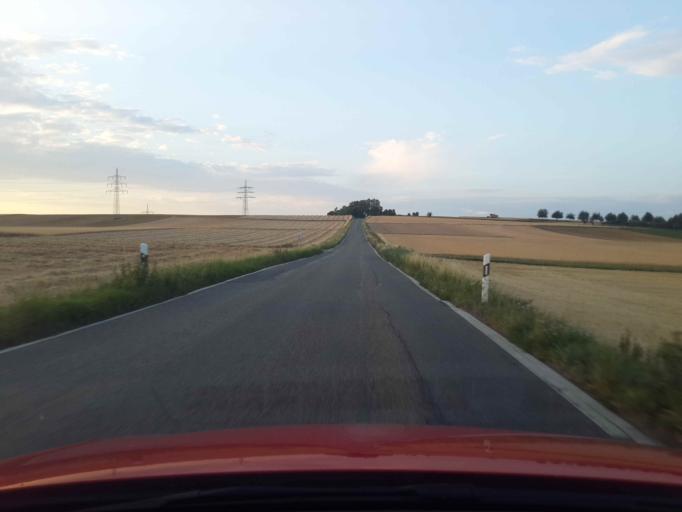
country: DE
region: Baden-Wuerttemberg
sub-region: Regierungsbezirk Stuttgart
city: Nordheim
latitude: 49.1198
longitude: 9.1296
